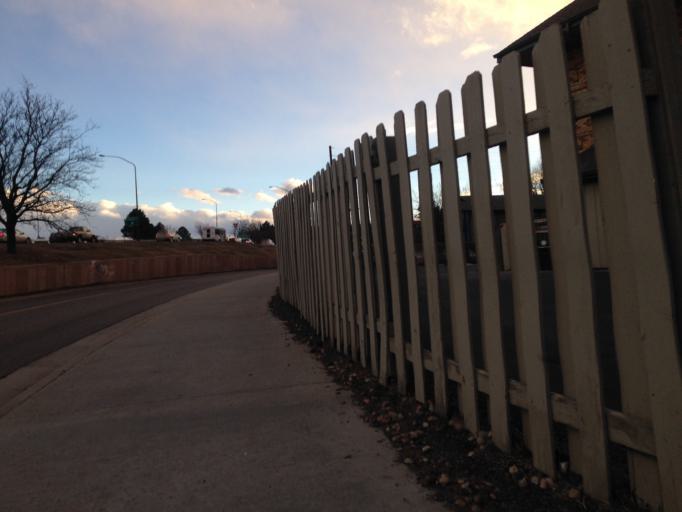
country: US
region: Colorado
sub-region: Boulder County
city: Boulder
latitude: 39.9888
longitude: -105.2321
